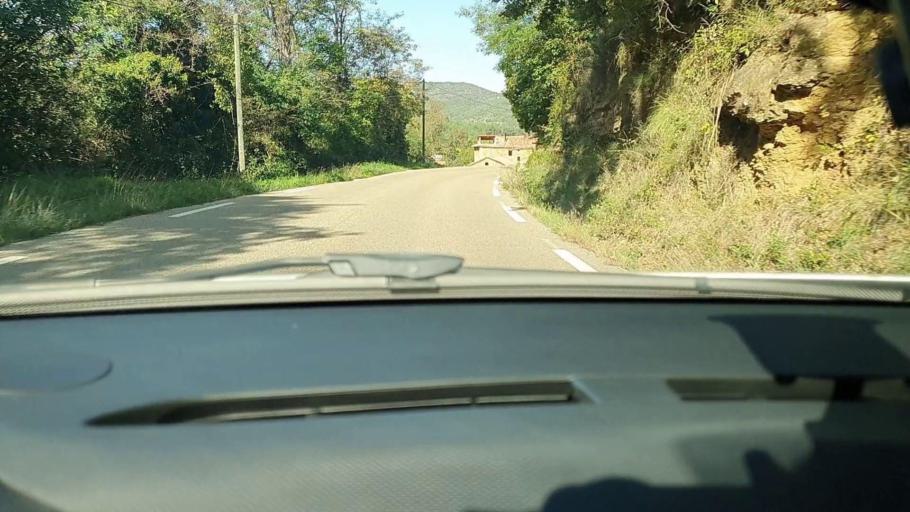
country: FR
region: Languedoc-Roussillon
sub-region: Departement du Gard
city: Molieres-sur-Ceze
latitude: 44.2554
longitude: 4.1379
